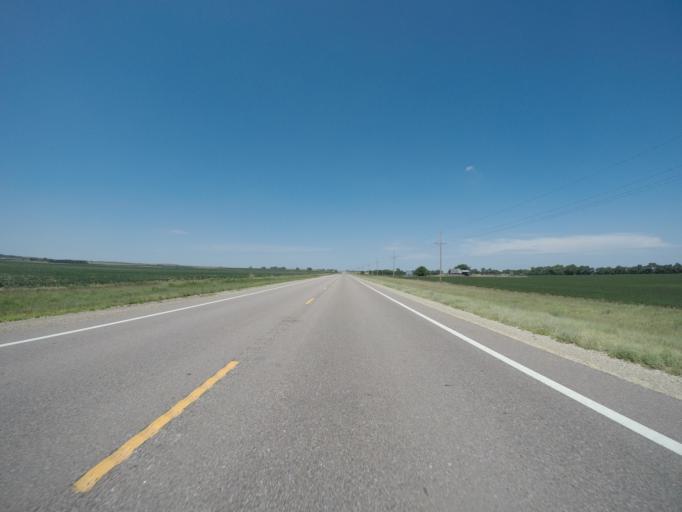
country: US
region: Kansas
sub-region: Osborne County
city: Osborne
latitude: 39.5098
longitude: -98.6290
